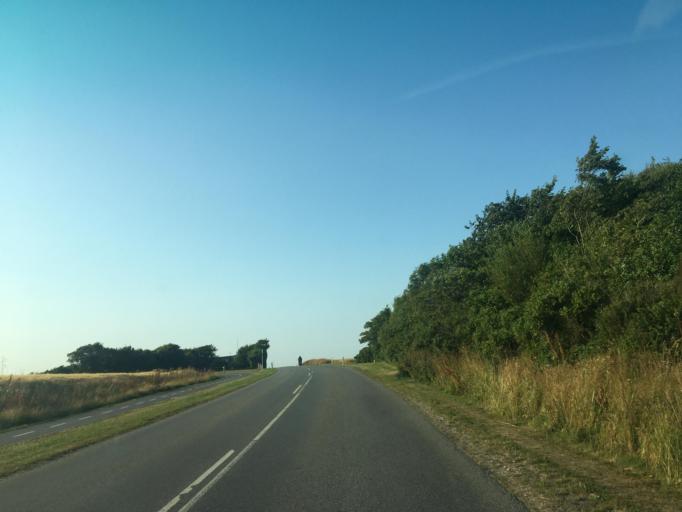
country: DK
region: North Denmark
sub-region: Thisted Kommune
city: Hurup
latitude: 56.7743
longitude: 8.4234
